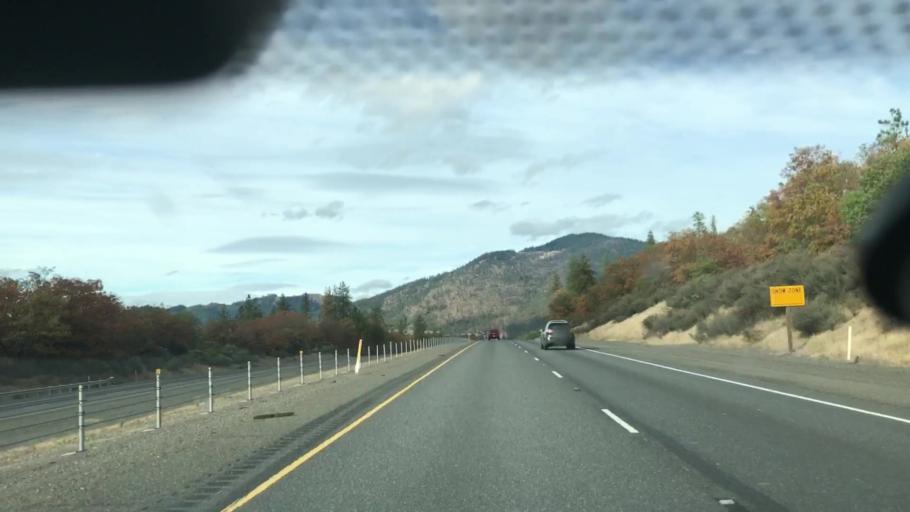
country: US
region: Oregon
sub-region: Josephine County
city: Merlin
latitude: 42.5404
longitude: -123.3700
